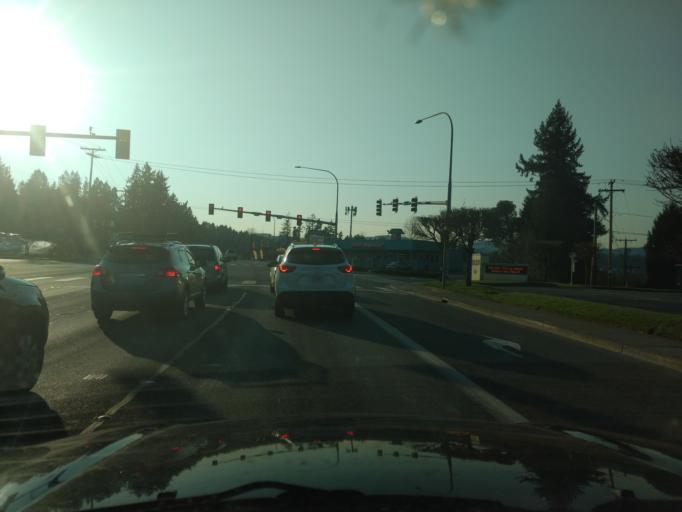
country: US
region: Washington
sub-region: Kitsap County
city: Navy Yard City
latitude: 47.5711
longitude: -122.6631
